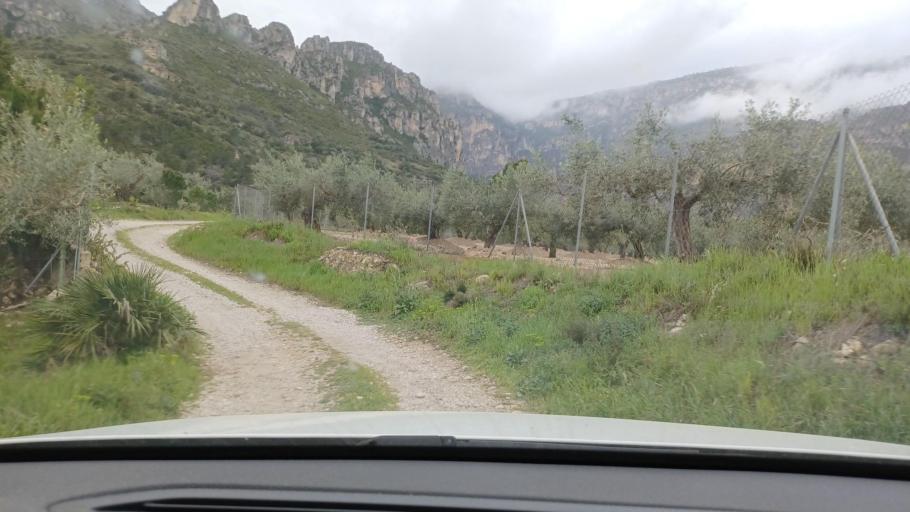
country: ES
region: Catalonia
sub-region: Provincia de Tarragona
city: Mas de Barberans
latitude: 40.8054
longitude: 0.4016
